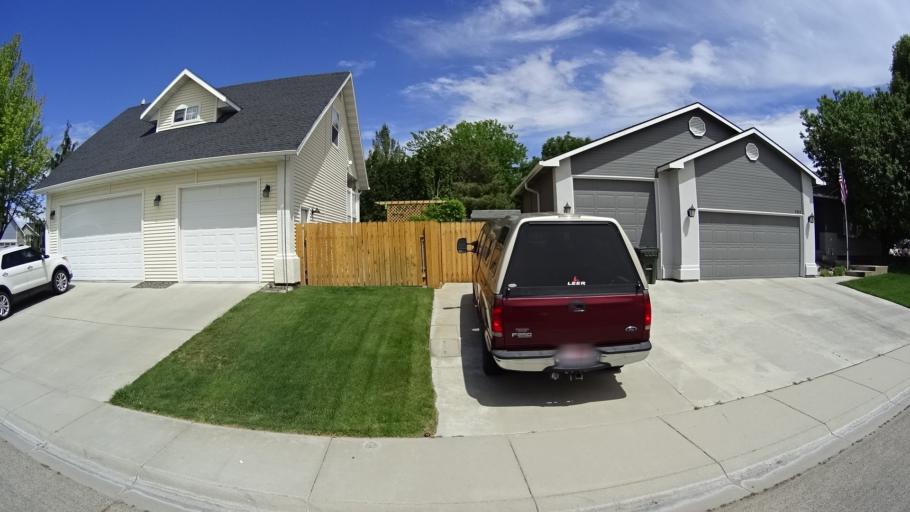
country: US
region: Idaho
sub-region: Ada County
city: Meridian
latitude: 43.5732
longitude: -116.4039
